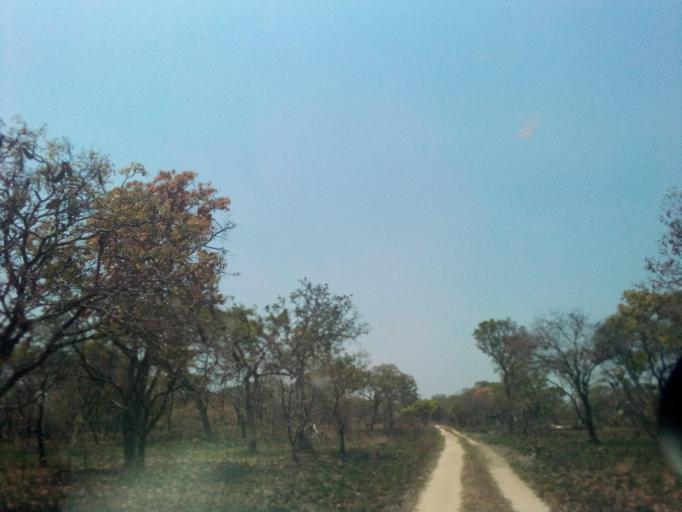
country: ZM
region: Copperbelt
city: Kataba
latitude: -12.2402
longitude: 30.4029
